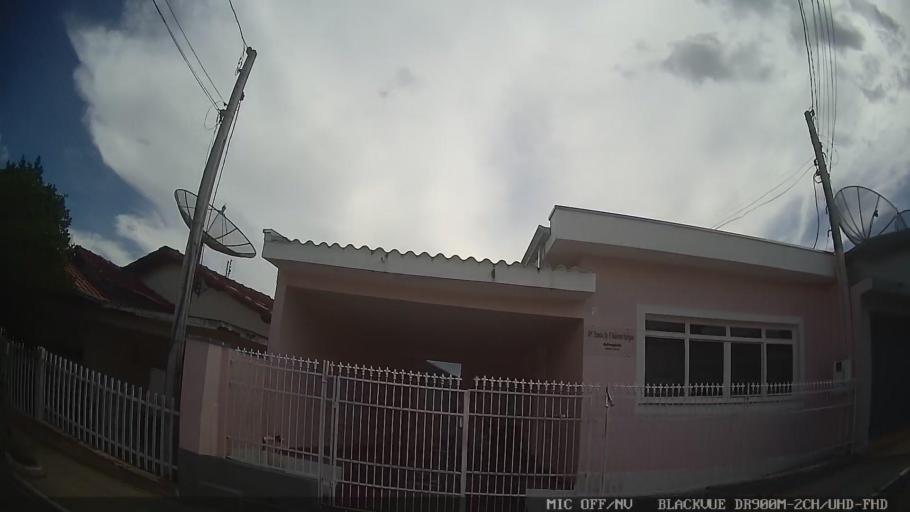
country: BR
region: Sao Paulo
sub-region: Conchas
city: Conchas
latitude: -23.0146
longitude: -48.0054
